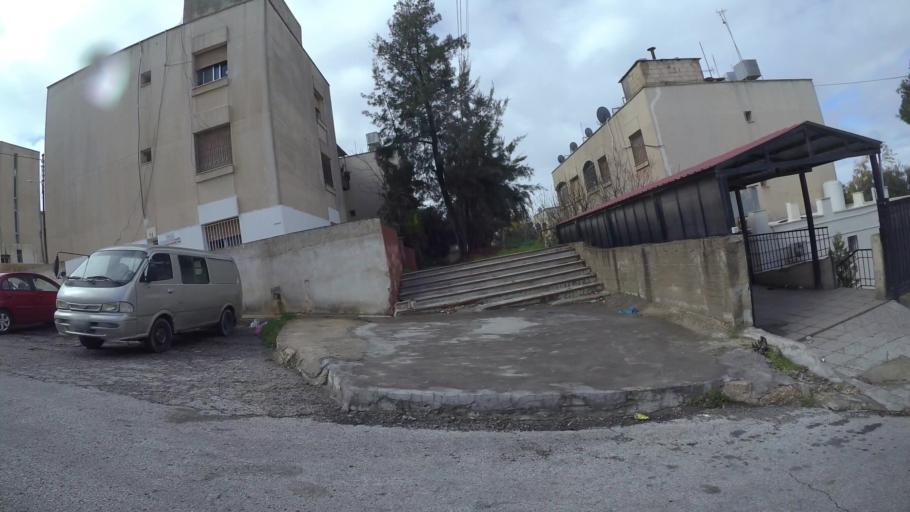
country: JO
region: Amman
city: Al Jubayhah
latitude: 32.0562
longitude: 35.8775
